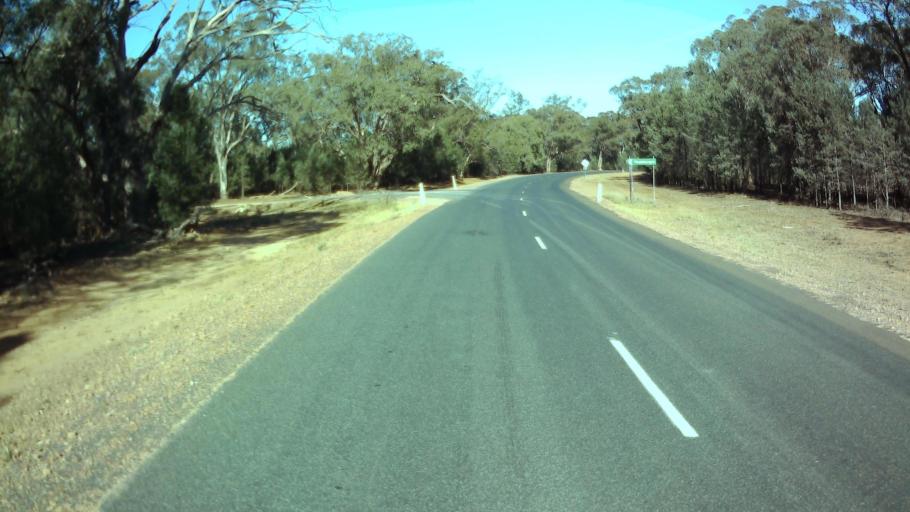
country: AU
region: New South Wales
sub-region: Weddin
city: Grenfell
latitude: -34.0353
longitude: 148.0837
